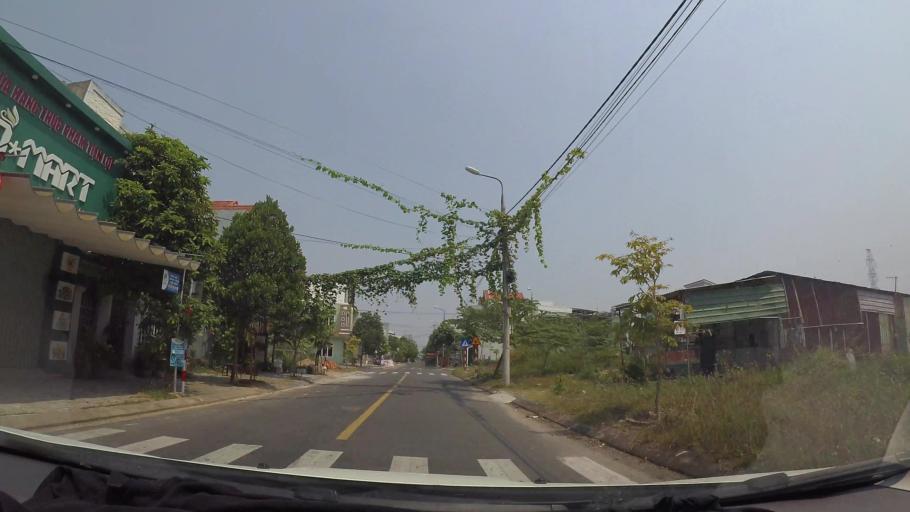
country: VN
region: Da Nang
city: Cam Le
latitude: 15.9958
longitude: 108.2017
